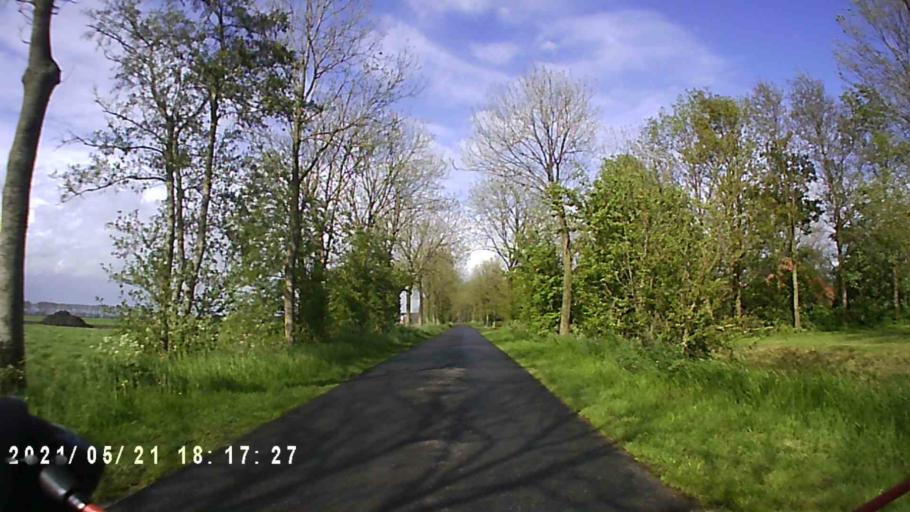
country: NL
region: Groningen
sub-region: Gemeente Zuidhorn
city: Zuidhorn
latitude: 53.2240
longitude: 6.4159
